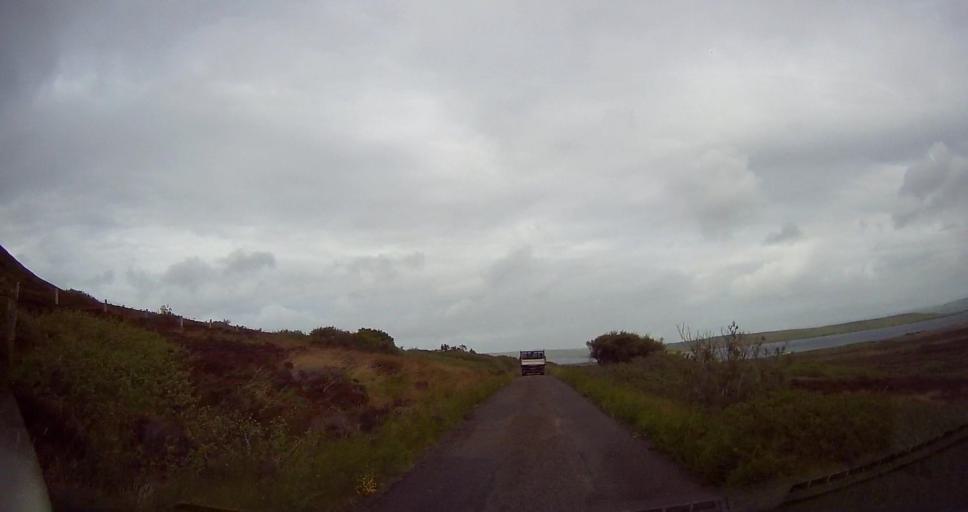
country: GB
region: Scotland
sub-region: Orkney Islands
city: Stromness
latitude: 58.8977
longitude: -3.3147
